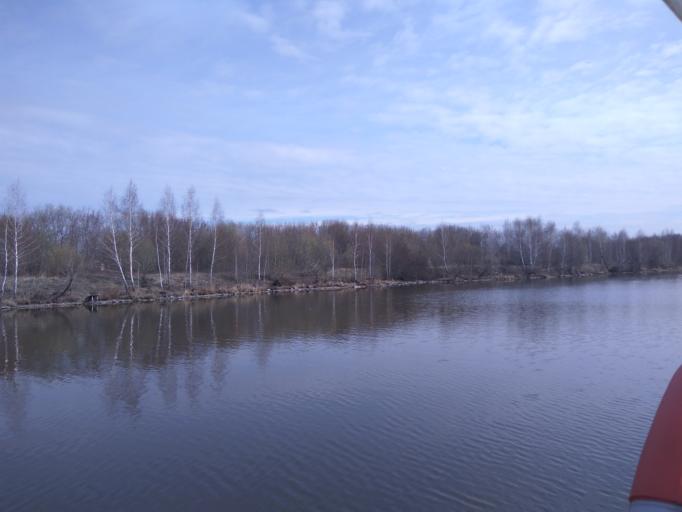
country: RU
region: Moscow
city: Kolomenskoye
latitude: 55.6918
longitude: 37.6930
